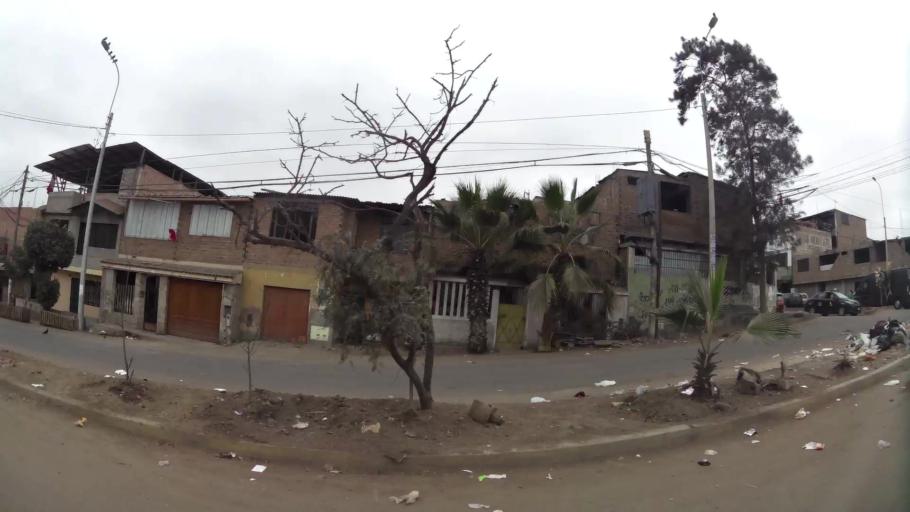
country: PE
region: Lima
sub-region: Lima
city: Surco
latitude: -12.1889
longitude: -76.9481
